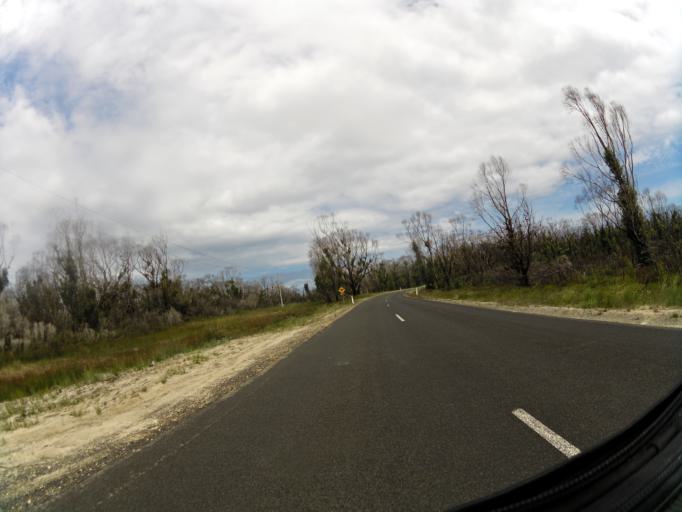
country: AU
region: Victoria
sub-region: East Gippsland
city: Lakes Entrance
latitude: -37.7963
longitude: 148.7327
